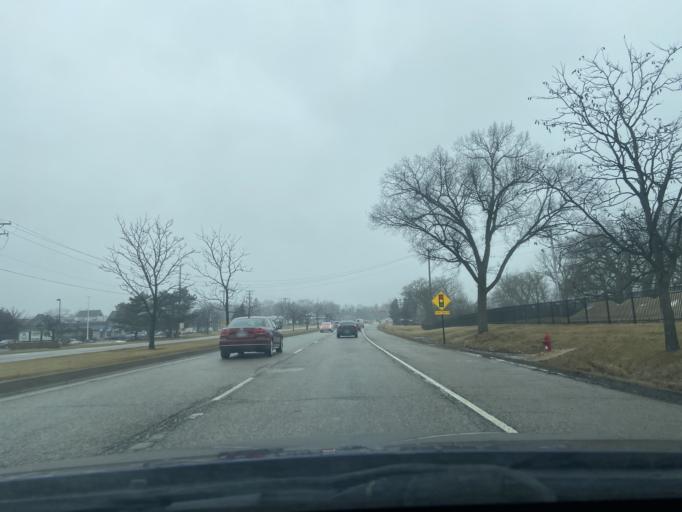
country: US
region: Illinois
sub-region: Lake County
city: Knollwood
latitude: 42.1952
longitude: -88.1100
